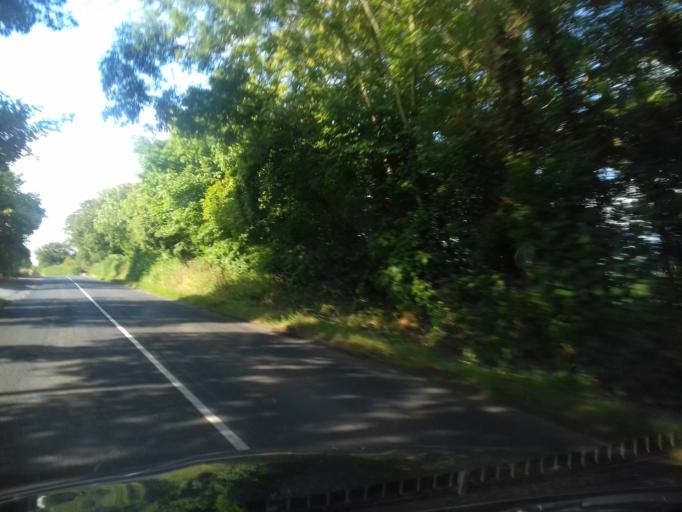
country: IE
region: Leinster
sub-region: Loch Garman
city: New Ross
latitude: 52.4460
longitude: -6.9627
